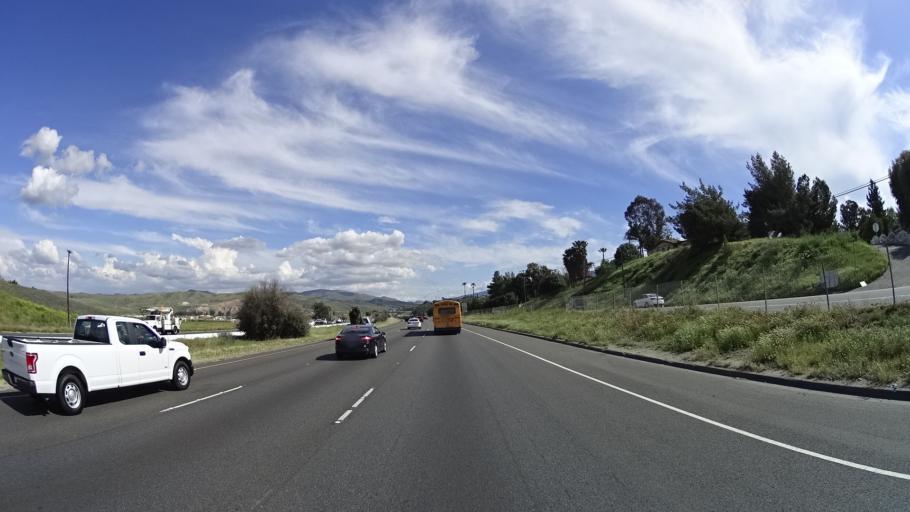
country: US
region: California
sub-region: Riverside County
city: El Cerrito
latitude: 33.8287
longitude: -117.5277
